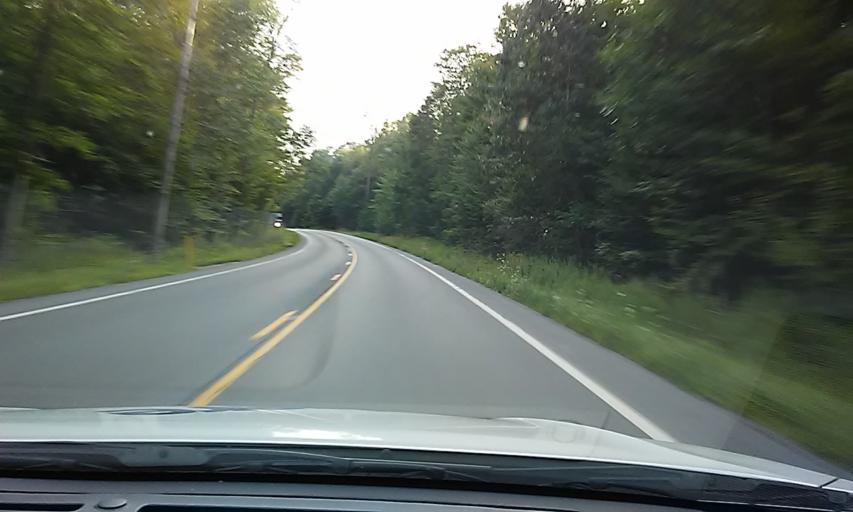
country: US
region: Pennsylvania
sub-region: McKean County
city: Kane
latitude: 41.5761
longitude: -78.8765
